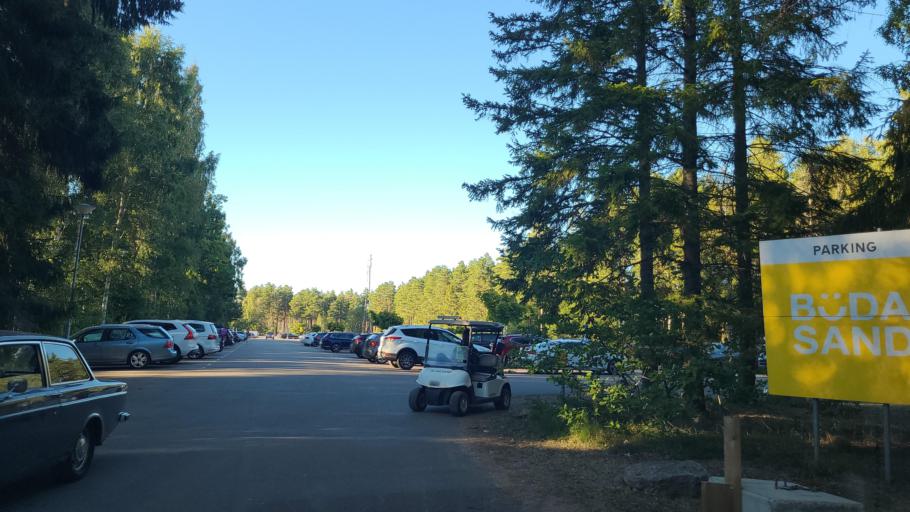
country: SE
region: Kalmar
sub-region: Borgholms Kommun
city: Borgholm
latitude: 57.2747
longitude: 17.0472
